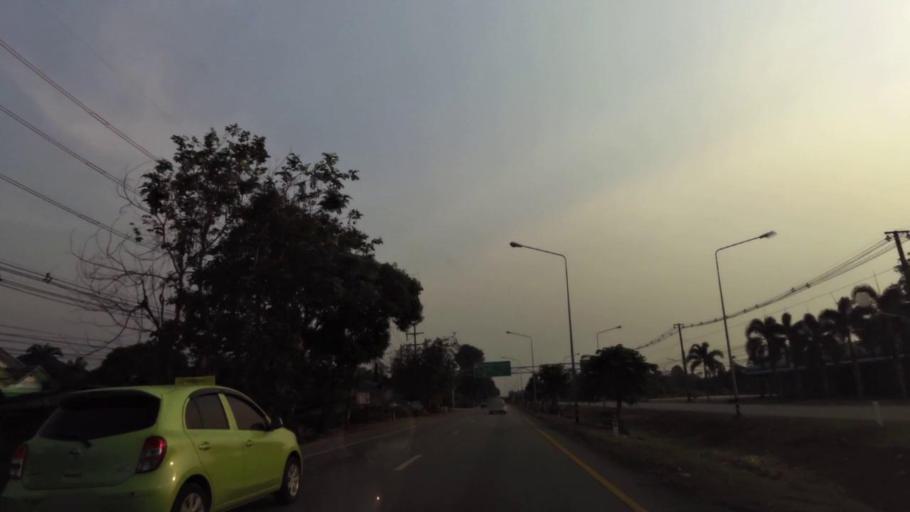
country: TH
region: Chanthaburi
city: Khlung
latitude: 12.5075
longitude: 102.1696
